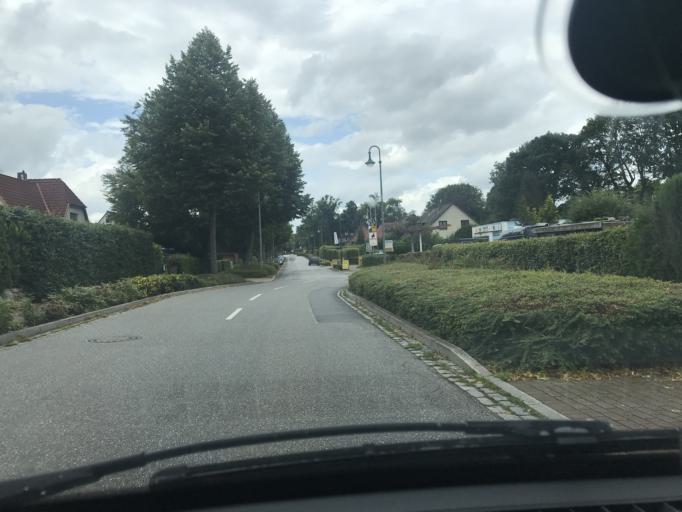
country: DE
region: Schleswig-Holstein
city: Grosshansdorf
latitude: 53.6519
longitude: 10.2657
